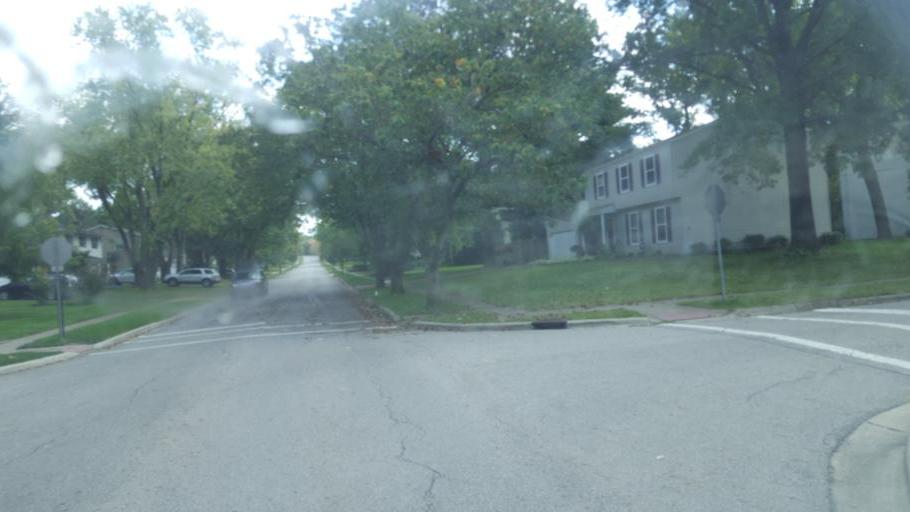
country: US
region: Ohio
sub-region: Franklin County
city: Worthington
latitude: 40.1057
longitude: -83.0249
